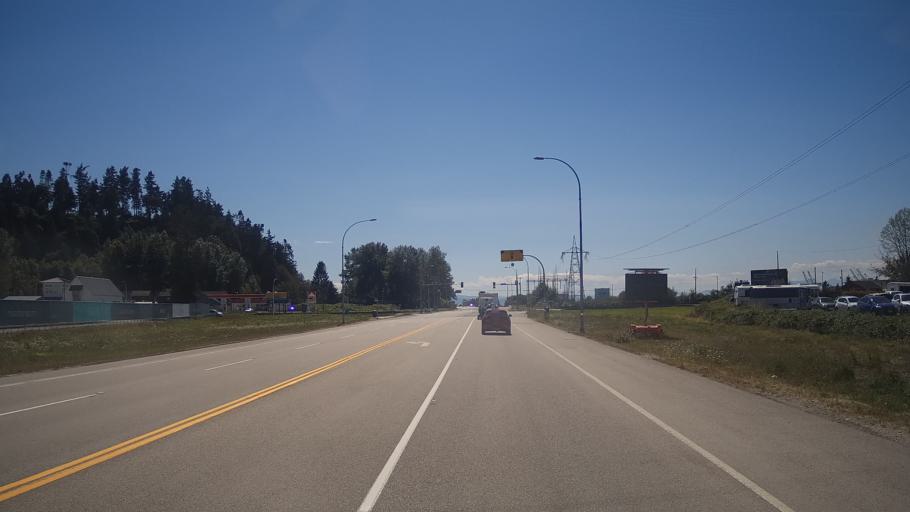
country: US
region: Washington
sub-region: Whatcom County
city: Point Roberts
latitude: 49.0302
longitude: -123.0950
